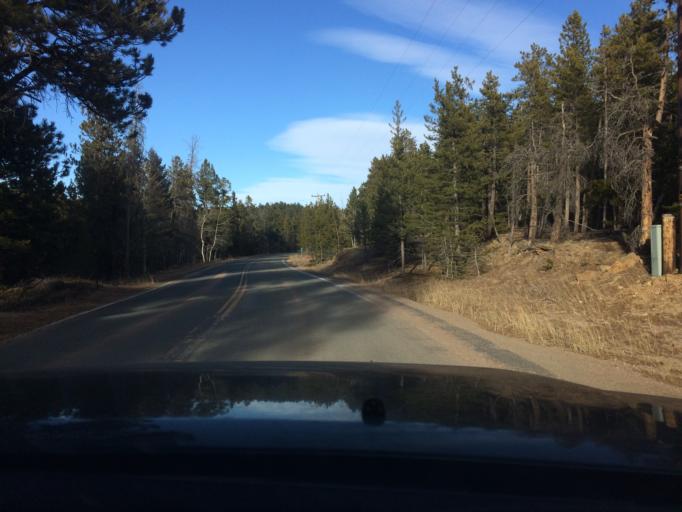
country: US
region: Colorado
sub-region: Boulder County
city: Nederland
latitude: 40.1266
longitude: -105.4348
